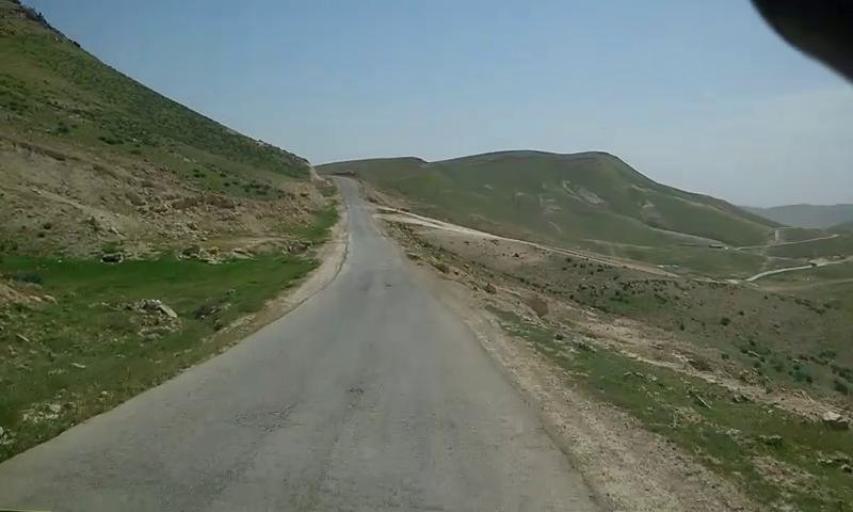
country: PS
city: `Arab ar Rashaydah
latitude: 31.5636
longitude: 35.2414
